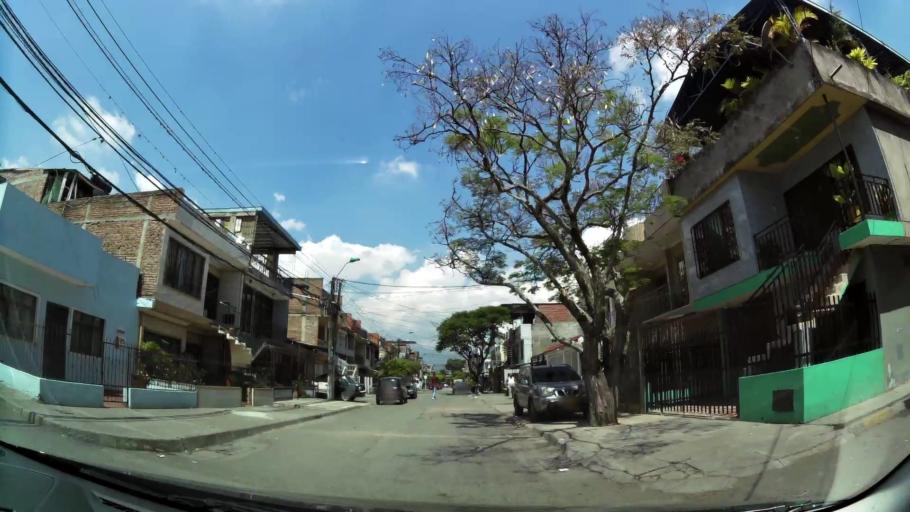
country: CO
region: Valle del Cauca
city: Cali
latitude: 3.4317
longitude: -76.5000
